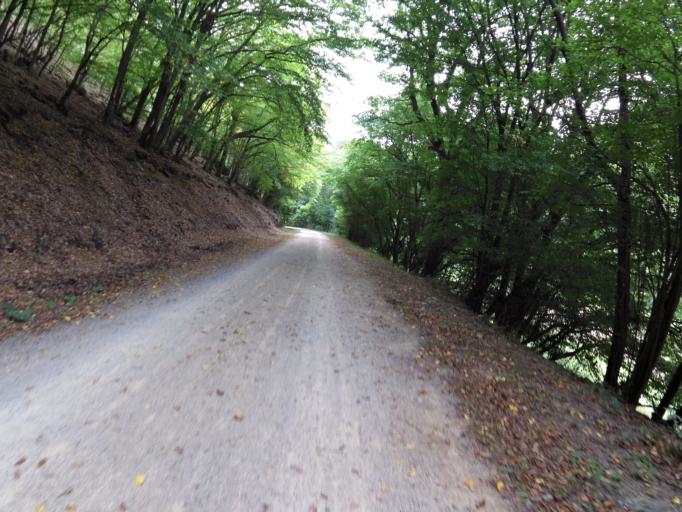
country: DE
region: North Rhine-Westphalia
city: Heimbach
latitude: 50.5834
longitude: 6.4621
